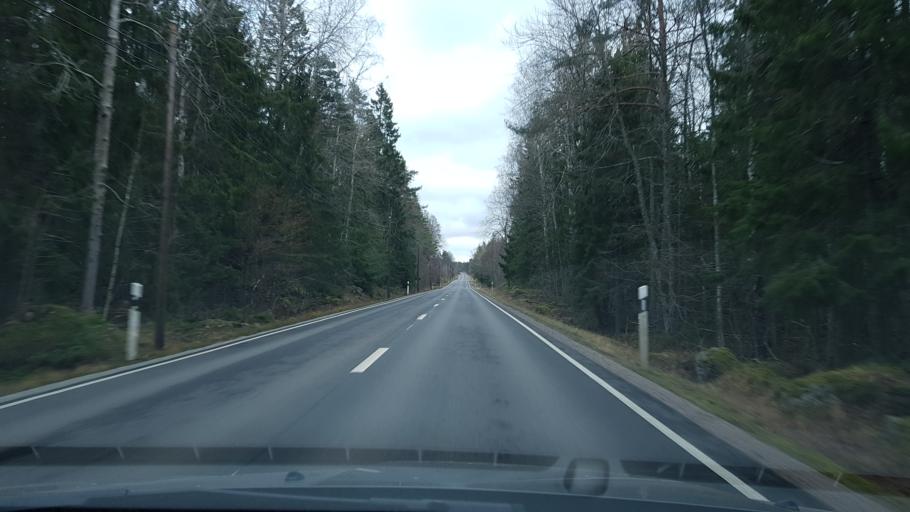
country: SE
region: Stockholm
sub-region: Norrtalje Kommun
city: Skanninge
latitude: 60.0176
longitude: 18.3643
